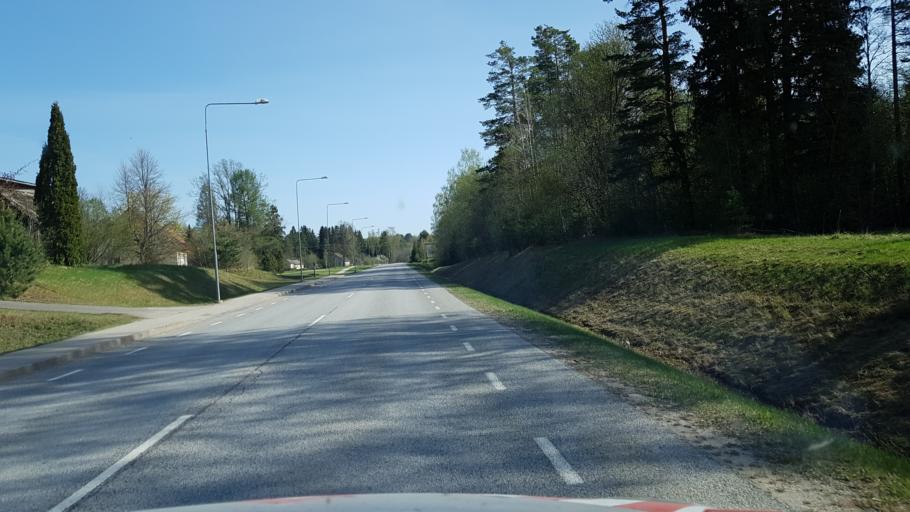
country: EE
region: Viljandimaa
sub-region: Abja vald
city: Abja-Paluoja
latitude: 58.1332
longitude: 25.3661
